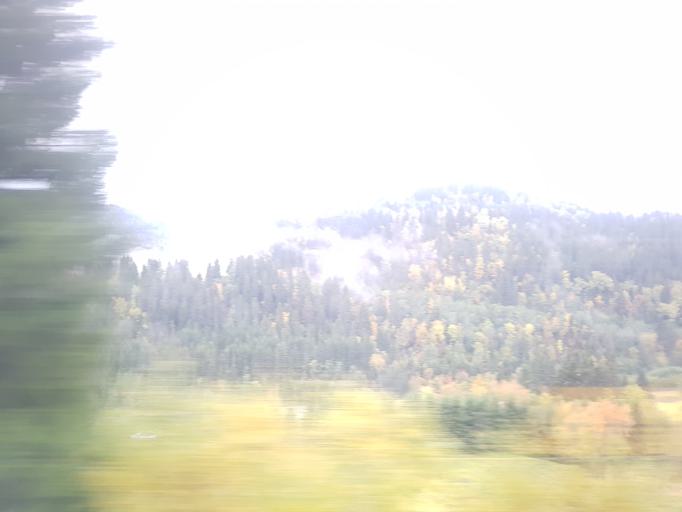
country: NO
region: Sor-Trondelag
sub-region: Midtre Gauldal
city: Storen
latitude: 62.9787
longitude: 10.2208
